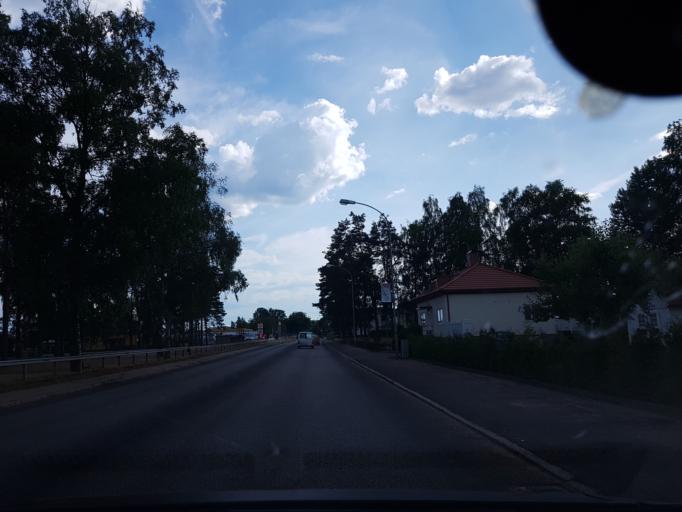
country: SE
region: Joenkoeping
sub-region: Gislaveds Kommun
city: Gislaved
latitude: 57.3093
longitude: 13.5434
